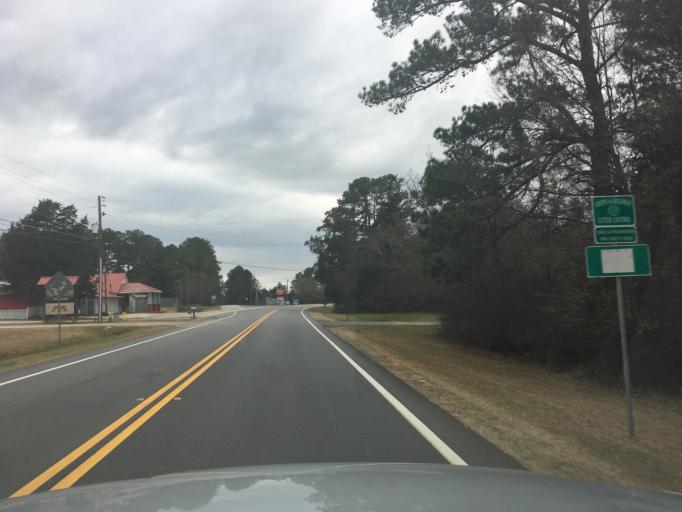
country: US
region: Georgia
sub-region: Columbia County
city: Appling
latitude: 33.6651
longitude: -82.3365
